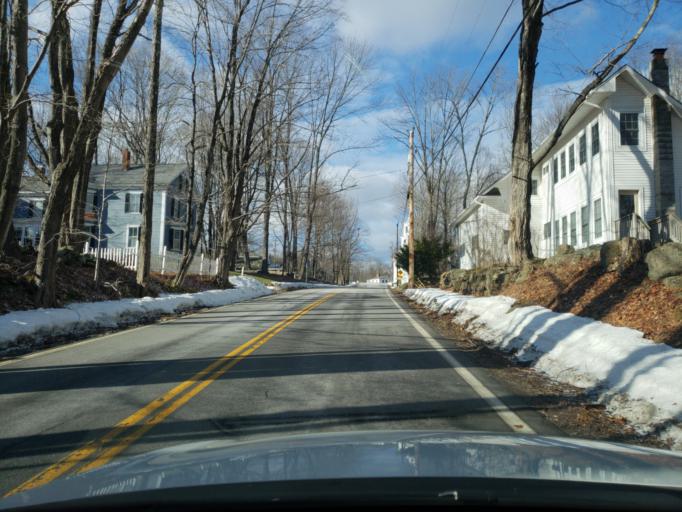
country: US
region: New Hampshire
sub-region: Hillsborough County
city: Greenfield
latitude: 42.9867
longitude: -71.8100
